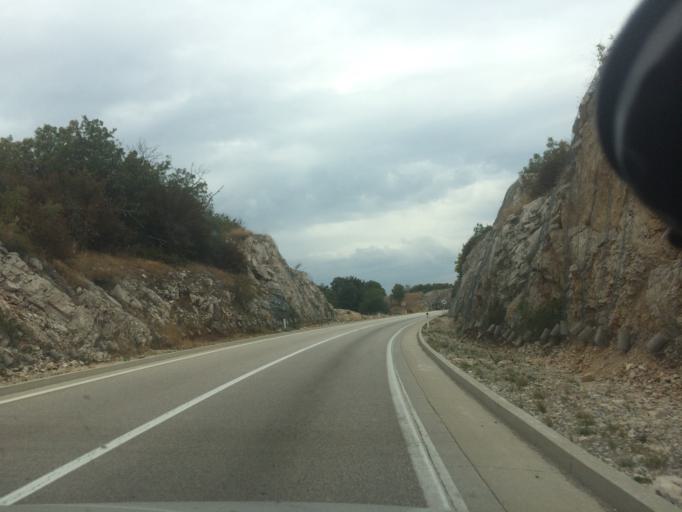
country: BA
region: Republika Srpska
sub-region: Opstina Bileca
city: Bileca
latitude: 42.7296
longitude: 18.6045
